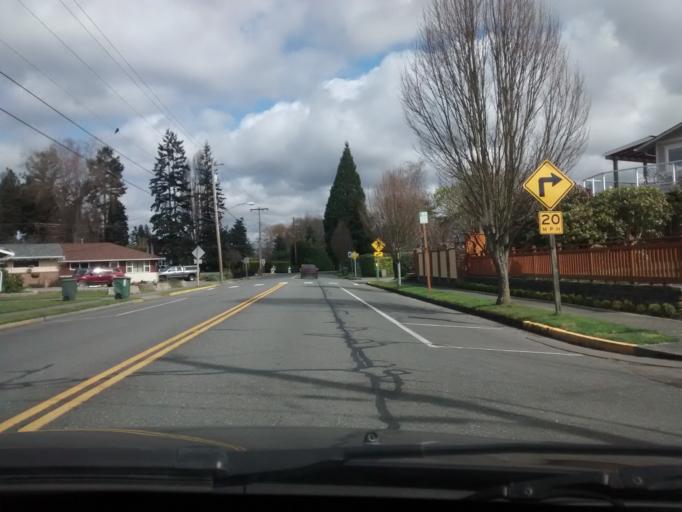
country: US
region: Washington
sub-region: Snohomish County
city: Edmonds
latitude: 47.8168
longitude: -122.3751
